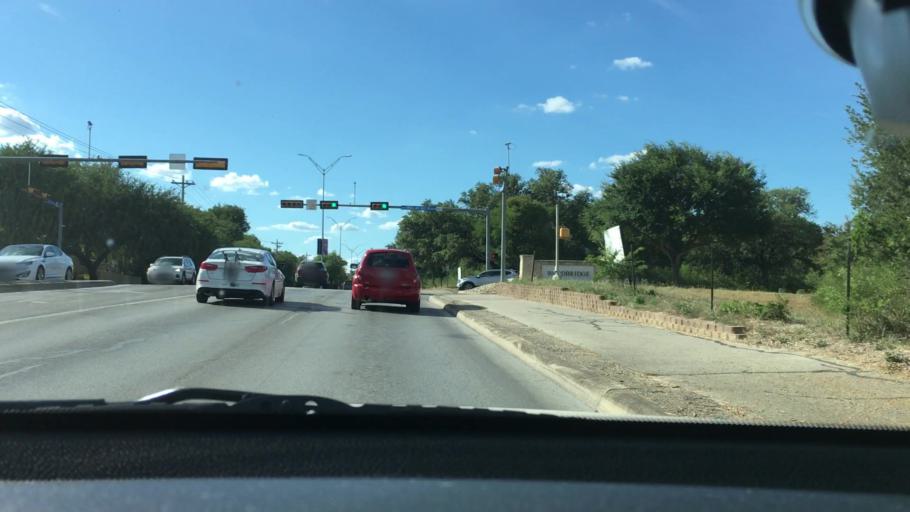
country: US
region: Texas
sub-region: Guadalupe County
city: Schertz
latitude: 29.5733
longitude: -98.2772
